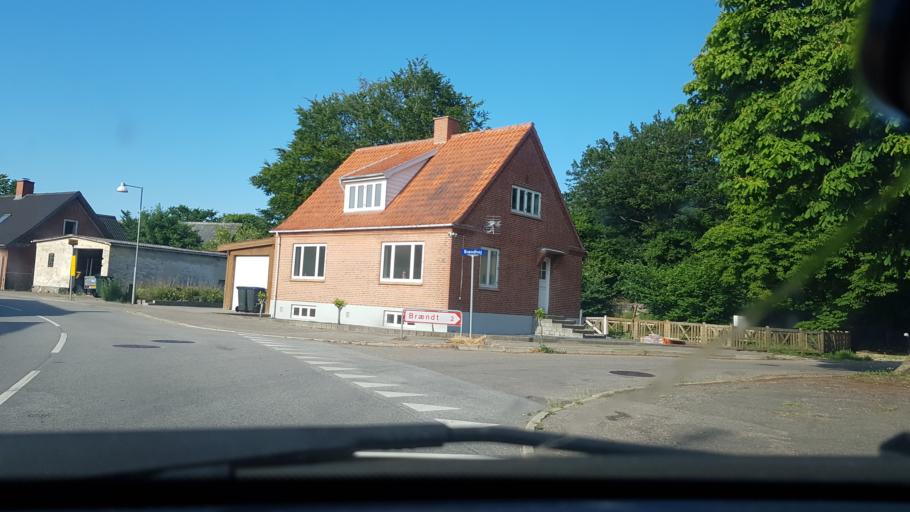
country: DK
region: Zealand
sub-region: Odsherred Kommune
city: Hojby
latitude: 55.8809
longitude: 11.6075
